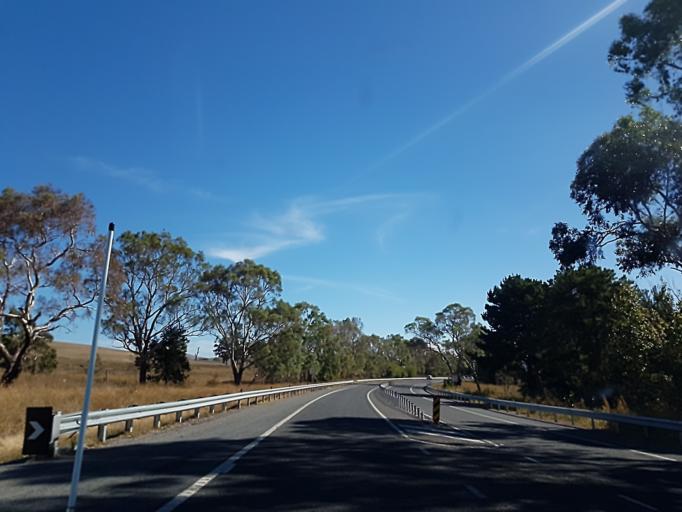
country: AU
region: Victoria
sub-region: Murrindindi
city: Alexandra
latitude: -37.2090
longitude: 145.4561
